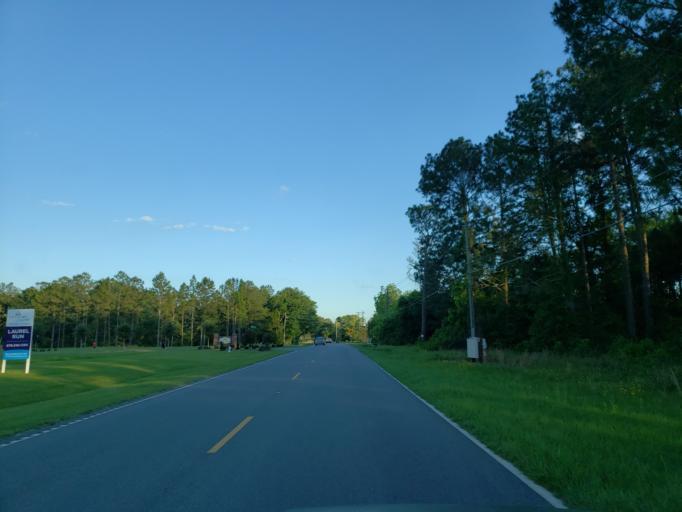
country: US
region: Georgia
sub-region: Lowndes County
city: Valdosta
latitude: 30.7649
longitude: -83.2656
